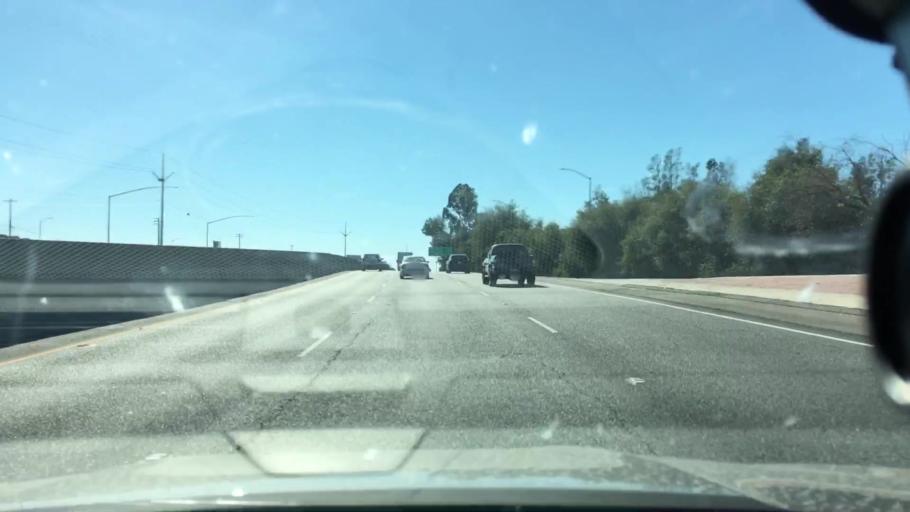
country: US
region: California
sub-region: Sacramento County
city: Arden-Arcade
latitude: 38.6303
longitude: -121.4029
